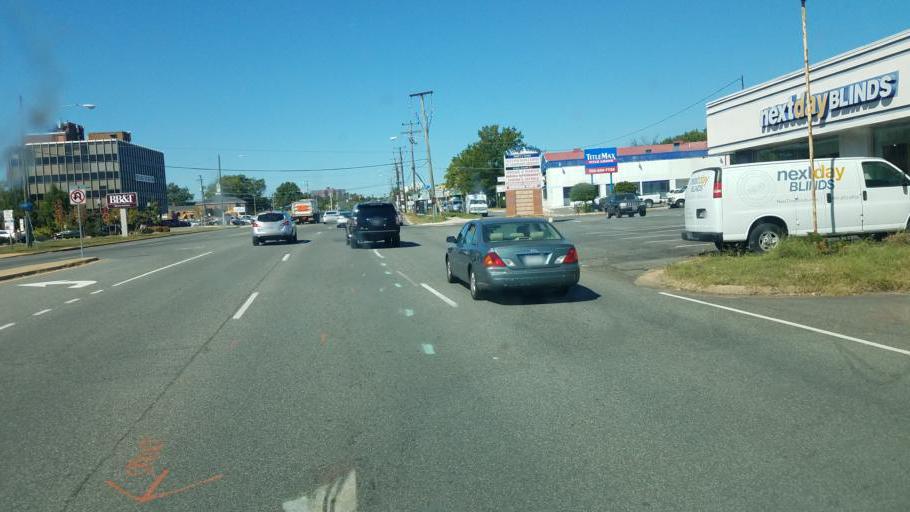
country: US
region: Virginia
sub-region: Fairfax County
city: Baileys Crossroads
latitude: 38.8522
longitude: -77.1326
